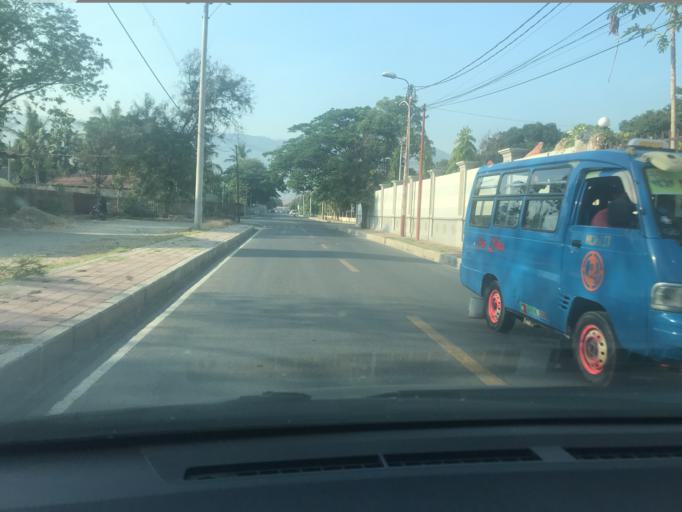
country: TL
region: Dili
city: Dili
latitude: -8.5497
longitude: 125.5683
